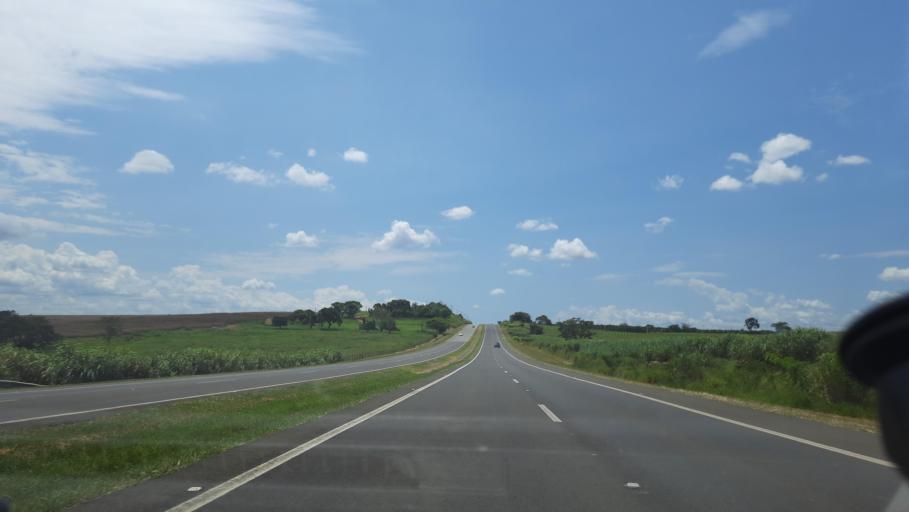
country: BR
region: Sao Paulo
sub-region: Mococa
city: Mococa
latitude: -21.6070
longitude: -47.0421
